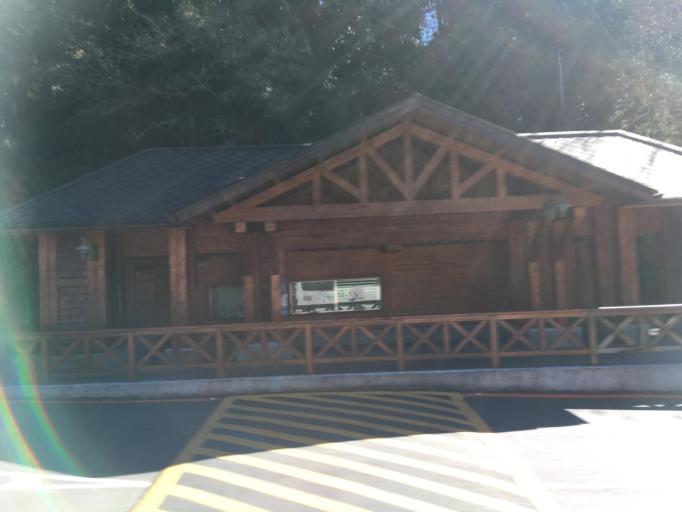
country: TW
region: Taiwan
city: Lugu
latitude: 23.5089
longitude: 120.8020
